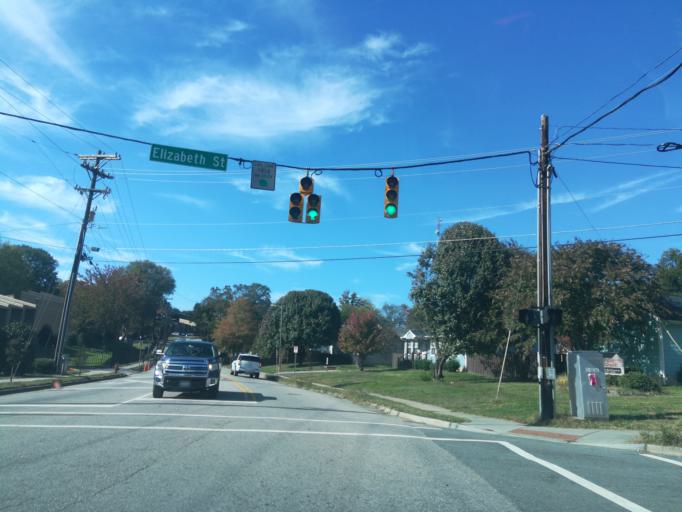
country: US
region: North Carolina
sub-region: Durham County
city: Durham
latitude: 35.9931
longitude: -78.8910
